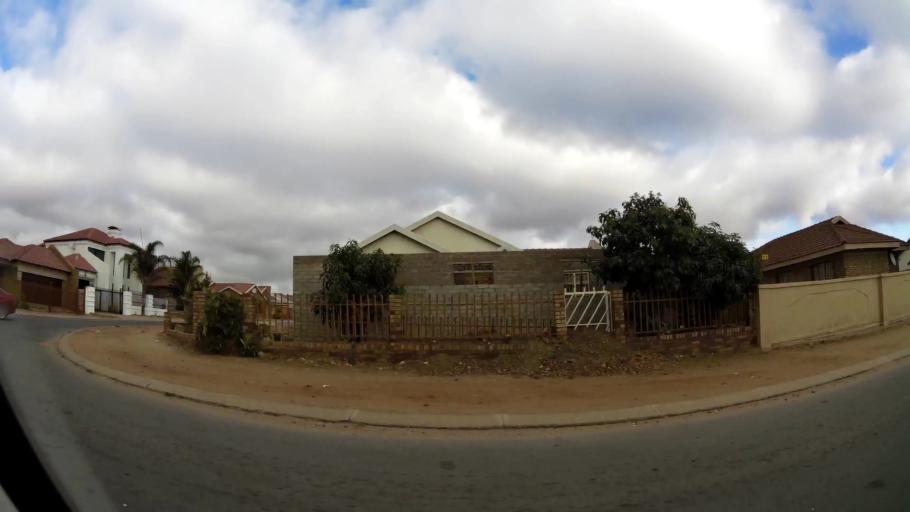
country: ZA
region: Limpopo
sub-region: Capricorn District Municipality
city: Polokwane
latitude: -23.9211
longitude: 29.4424
